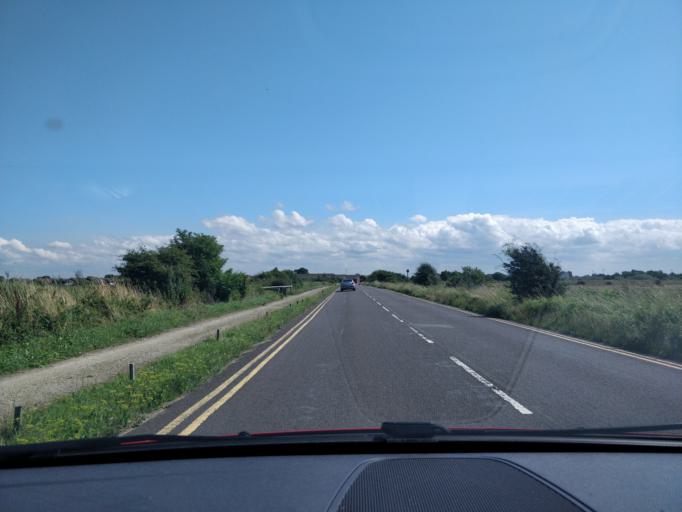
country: GB
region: England
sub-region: Sefton
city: Southport
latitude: 53.6744
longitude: -2.9785
